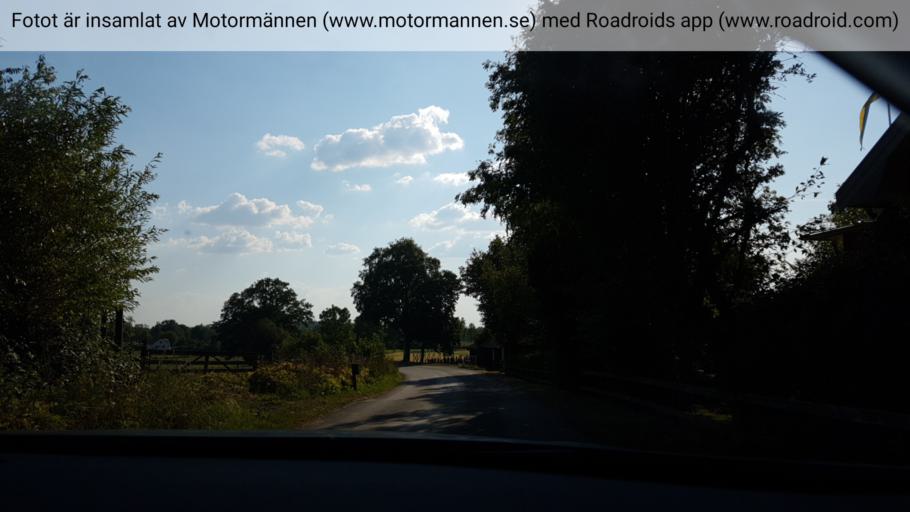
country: SE
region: Vaestra Goetaland
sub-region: Skovde Kommun
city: Stopen
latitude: 58.4899
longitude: 13.7761
